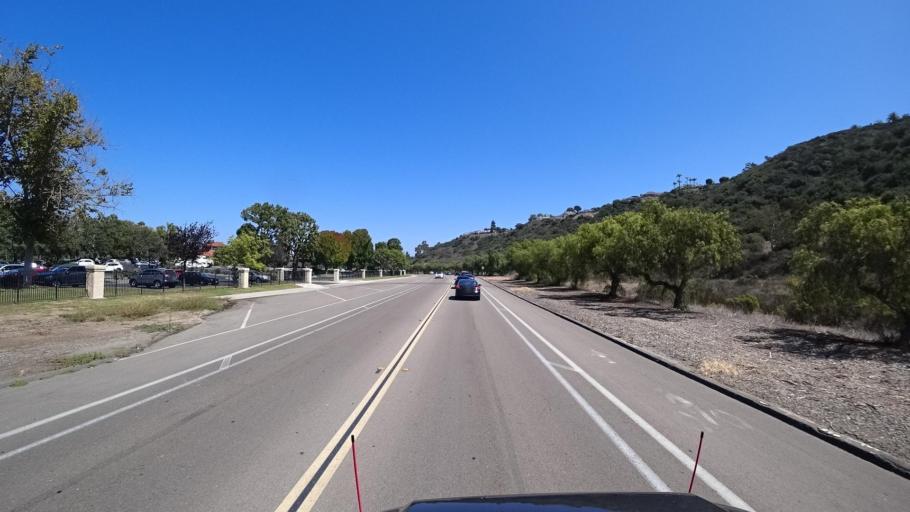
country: US
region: California
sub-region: San Diego County
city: Fairbanks Ranch
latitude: 32.9756
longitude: -117.2130
